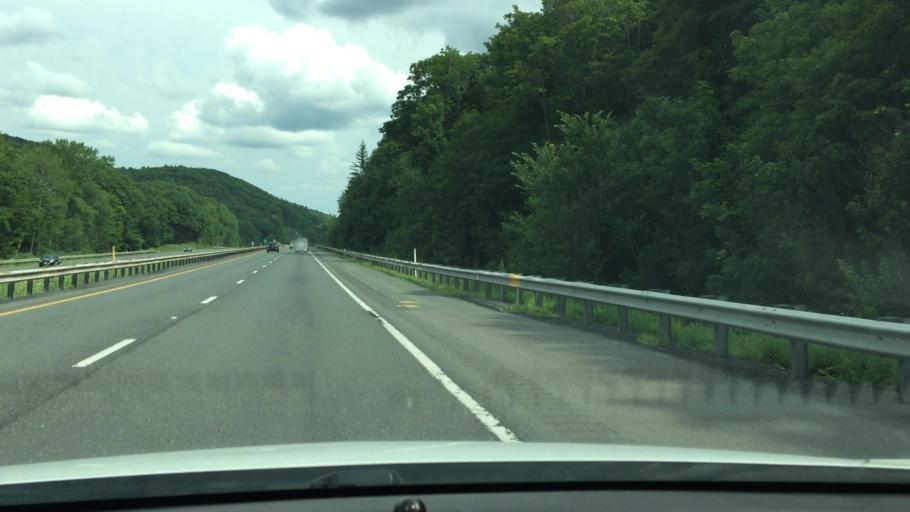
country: US
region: Massachusetts
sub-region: Berkshire County
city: Becket
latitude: 42.2811
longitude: -73.1489
